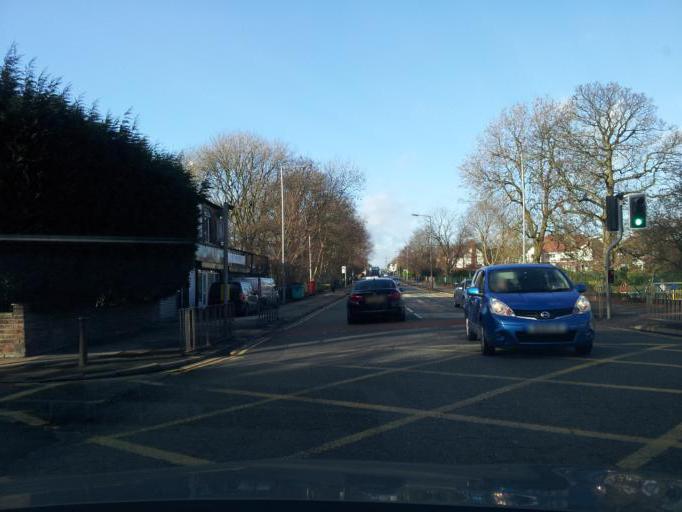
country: GB
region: England
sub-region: Borough of Bury
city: Prestwich
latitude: 53.5275
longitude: -2.2801
